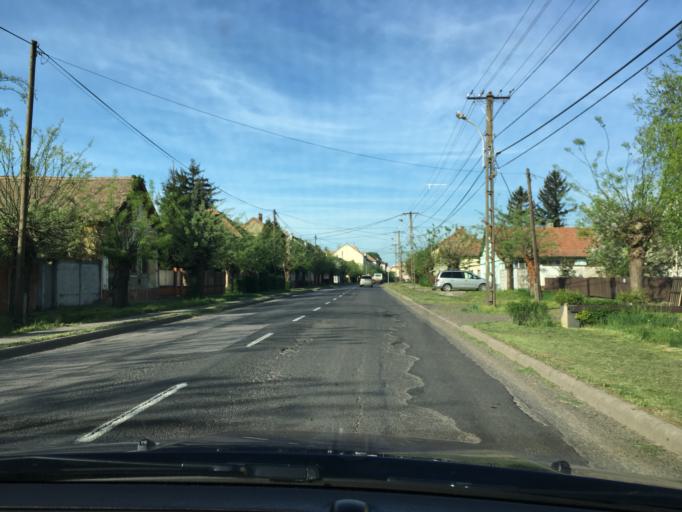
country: HU
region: Bekes
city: Mezobereny
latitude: 46.8192
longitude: 21.0250
